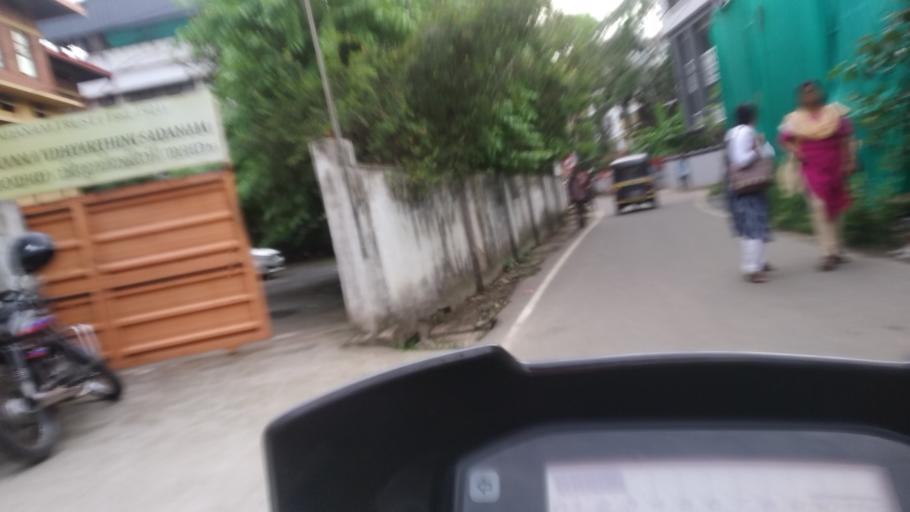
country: IN
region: Kerala
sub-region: Ernakulam
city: Cochin
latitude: 9.9678
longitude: 76.2876
